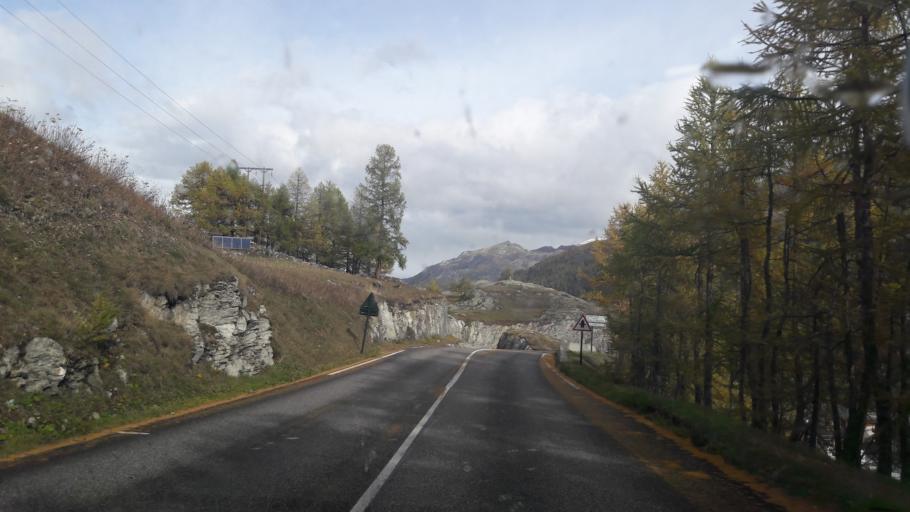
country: FR
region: Rhone-Alpes
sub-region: Departement de la Savoie
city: Tignes
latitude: 45.4915
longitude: 6.9253
